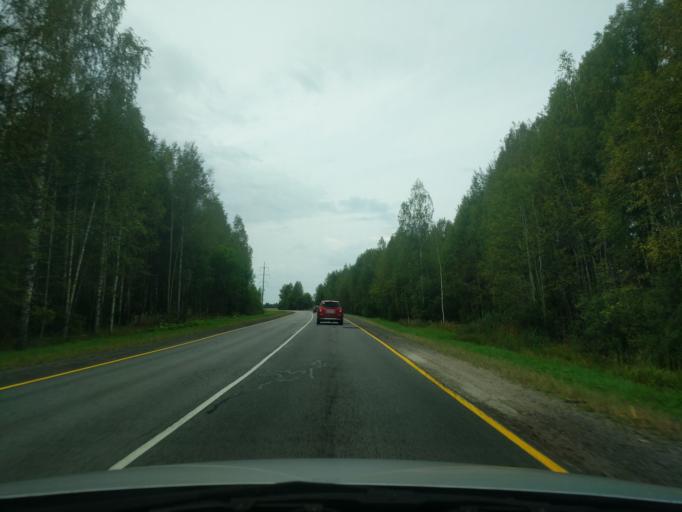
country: RU
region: Kirov
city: Kotel'nich
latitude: 58.2713
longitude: 48.0726
